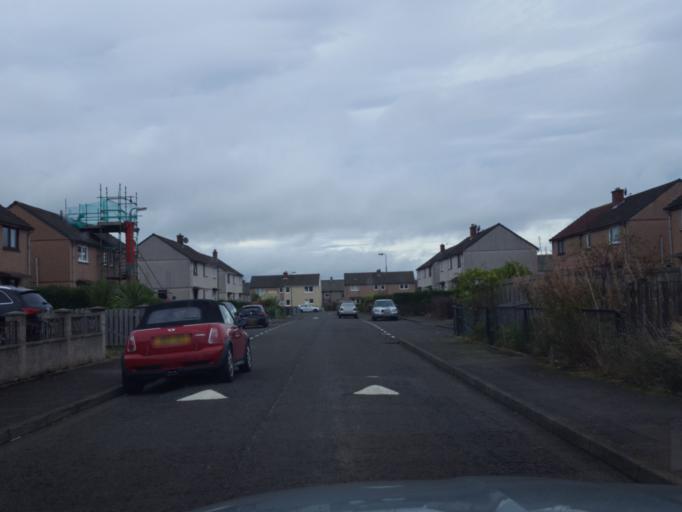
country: GB
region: Scotland
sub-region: Midlothian
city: Penicuik
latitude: 55.8328
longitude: -3.2139
